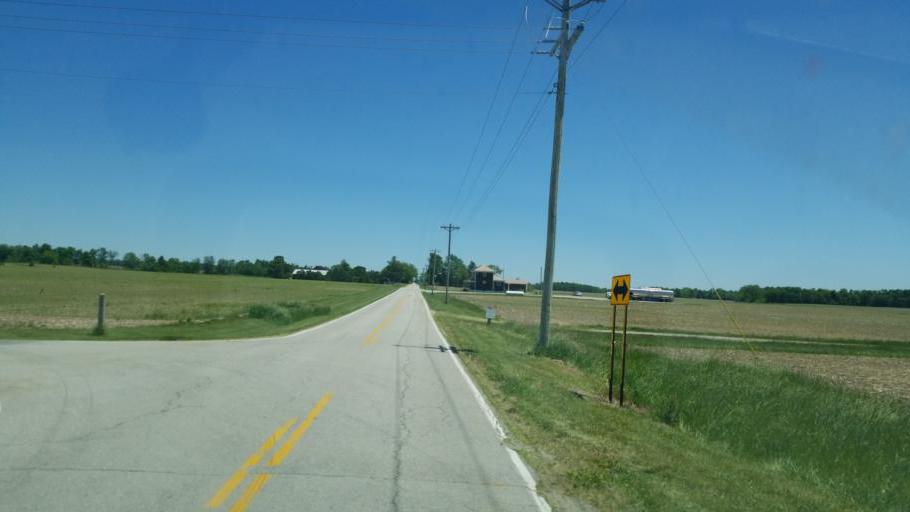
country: US
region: Ohio
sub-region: Darke County
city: Ansonia
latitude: 40.2648
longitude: -84.6756
